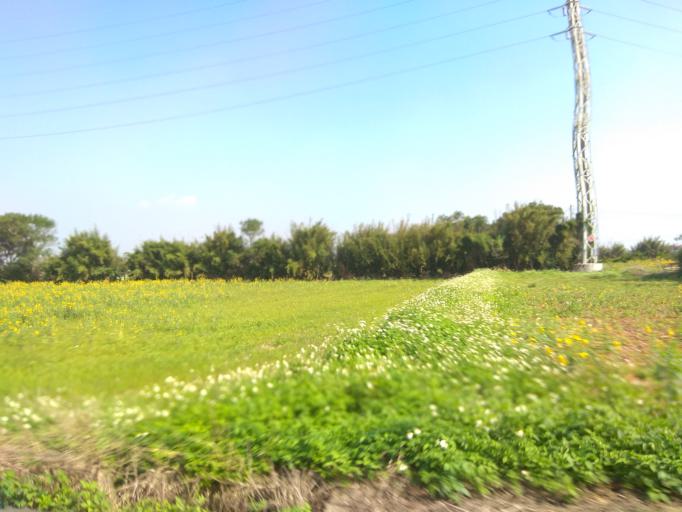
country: TW
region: Taiwan
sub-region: Hsinchu
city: Zhubei
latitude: 24.9866
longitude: 121.0764
